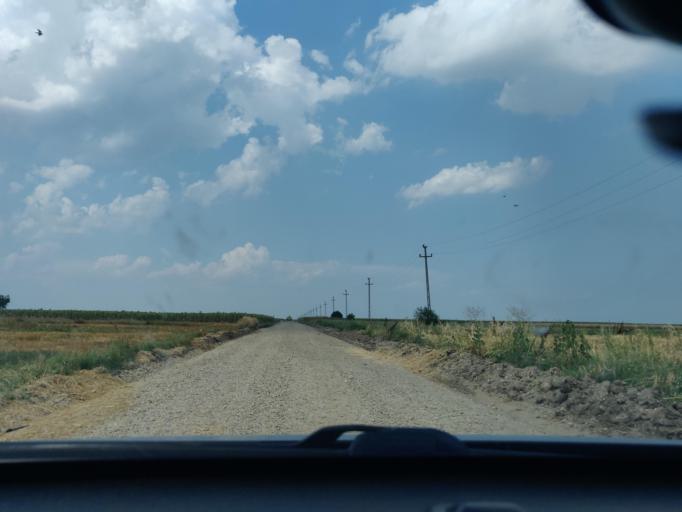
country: RO
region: Teleorman
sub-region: Comuna Sarbeni
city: Sarbeni
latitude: 44.4814
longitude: 25.3883
